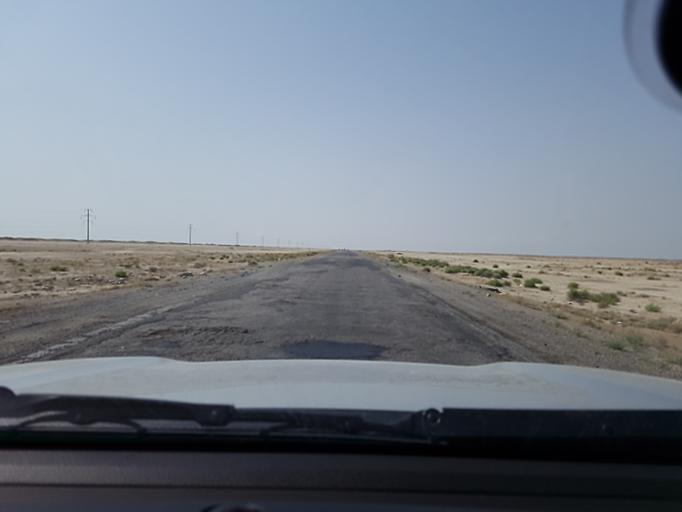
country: TM
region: Balkan
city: Gumdag
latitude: 38.8290
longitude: 54.5967
